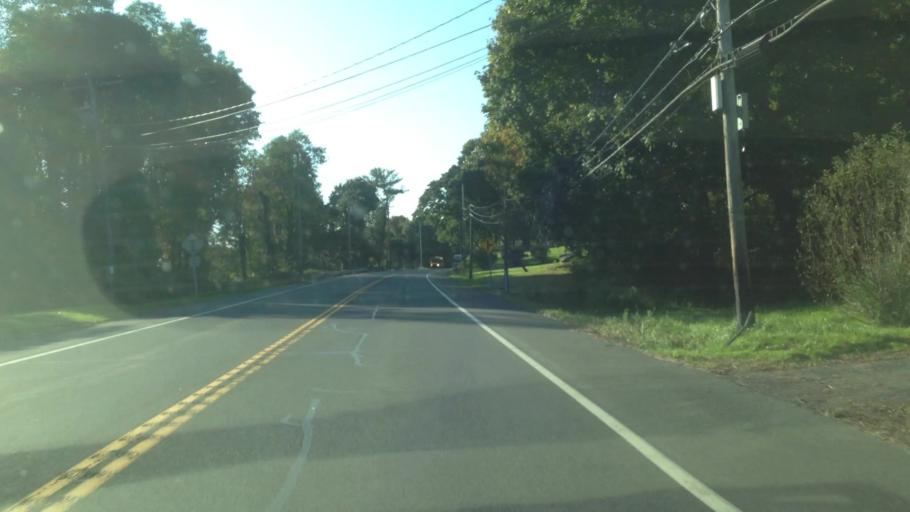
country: US
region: New York
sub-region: Dutchess County
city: Hyde Park
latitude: 41.7896
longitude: -73.9601
